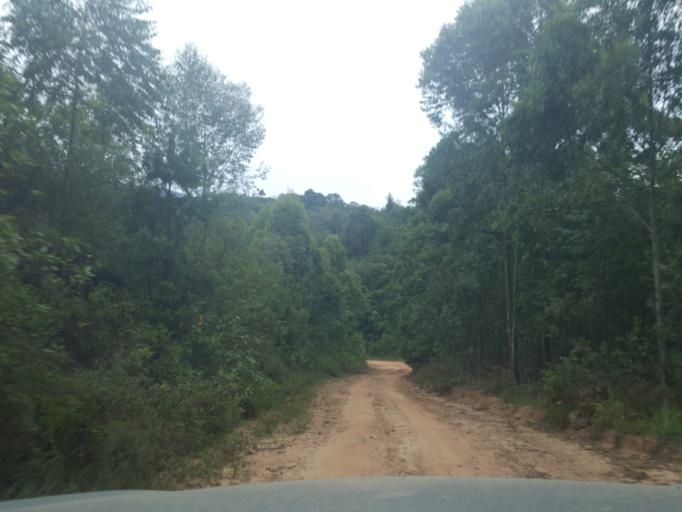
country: ZA
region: Limpopo
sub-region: Mopani District Municipality
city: Hoedspruit
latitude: -24.5855
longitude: 30.8639
